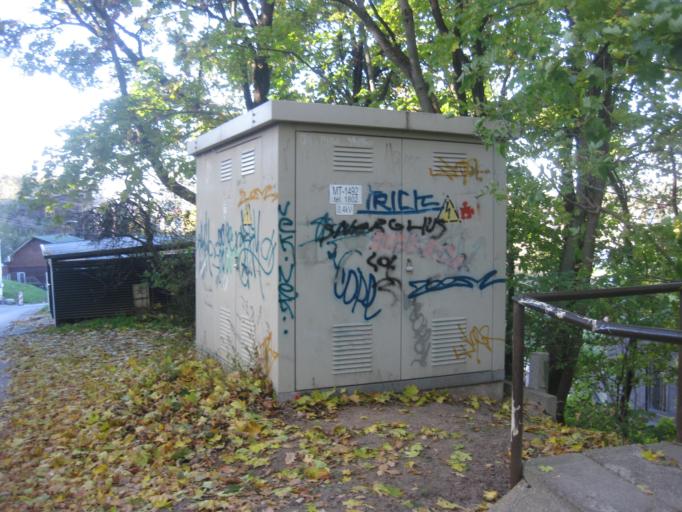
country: LT
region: Kauno apskritis
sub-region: Kaunas
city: Aleksotas
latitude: 54.8886
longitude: 23.8989
